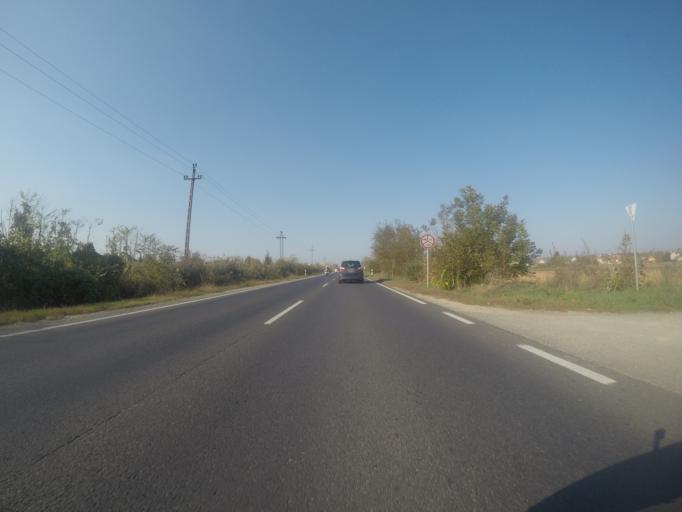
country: HU
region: Tolna
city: Dunafoldvar
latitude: 46.8063
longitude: 18.9144
